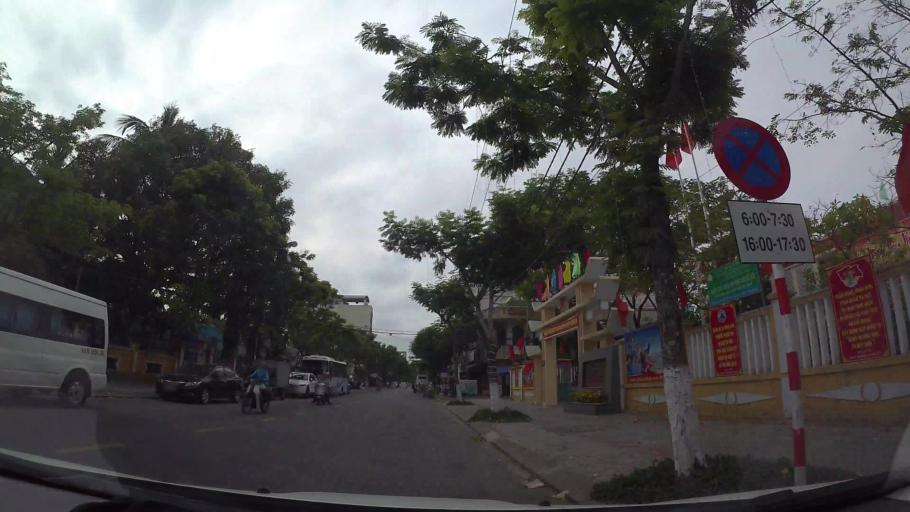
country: VN
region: Da Nang
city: Son Tra
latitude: 16.0647
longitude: 108.2425
